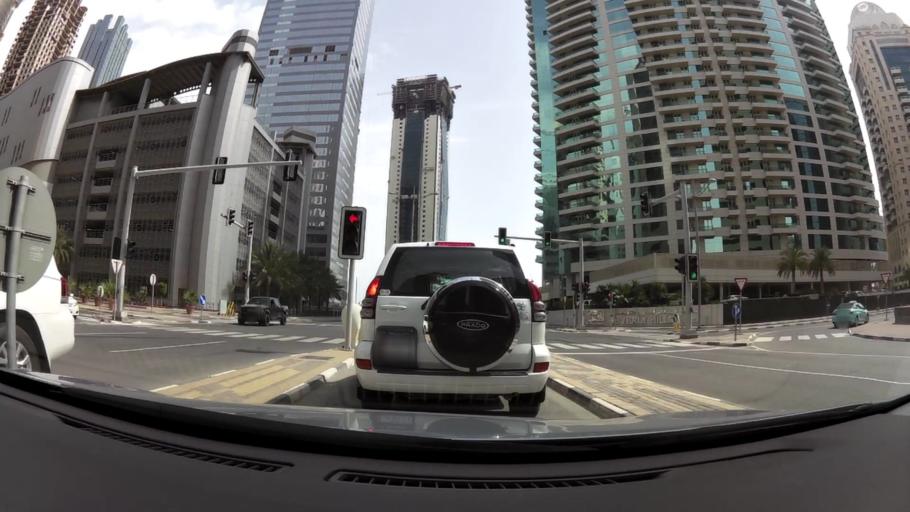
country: QA
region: Baladiyat ad Dawhah
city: Doha
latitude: 25.3259
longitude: 51.5345
